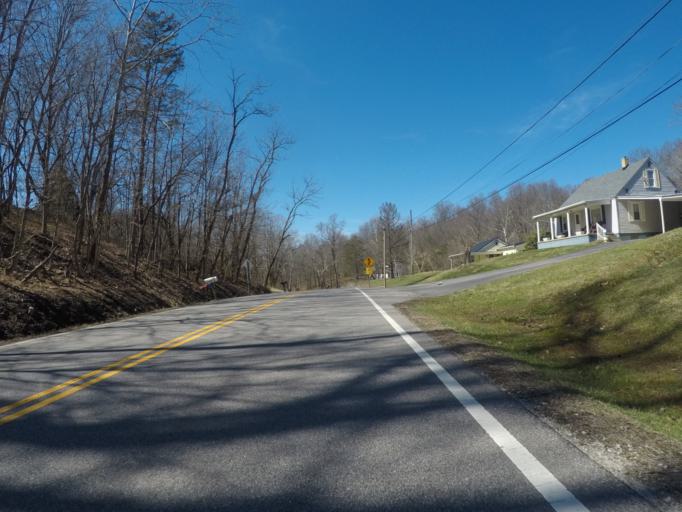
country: US
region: Ohio
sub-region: Lawrence County
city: South Point
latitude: 38.4878
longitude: -82.5529
